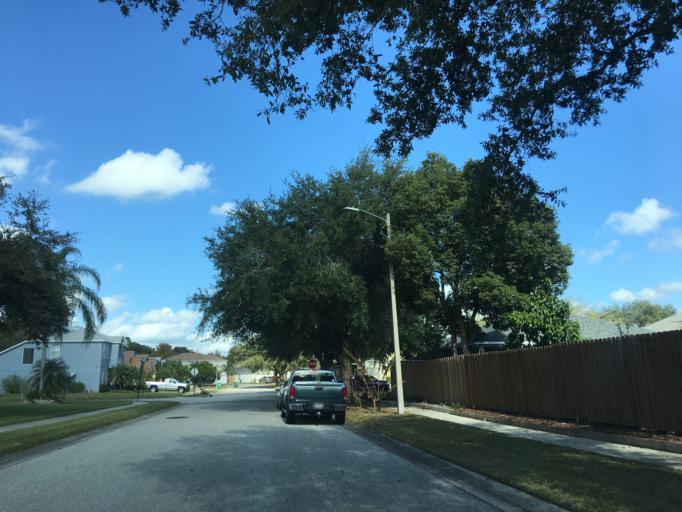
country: US
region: Florida
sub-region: Orange County
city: Eatonville
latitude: 28.6294
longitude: -81.4074
